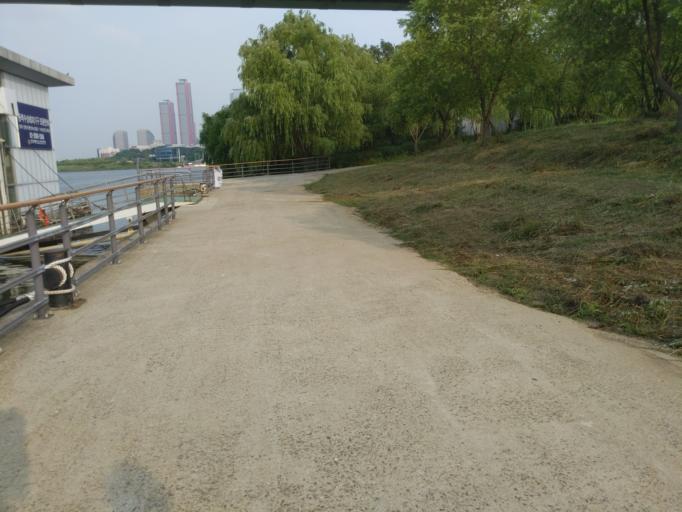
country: KR
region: Gyeonggi-do
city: Kwangmyong
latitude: 37.5381
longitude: 126.9045
